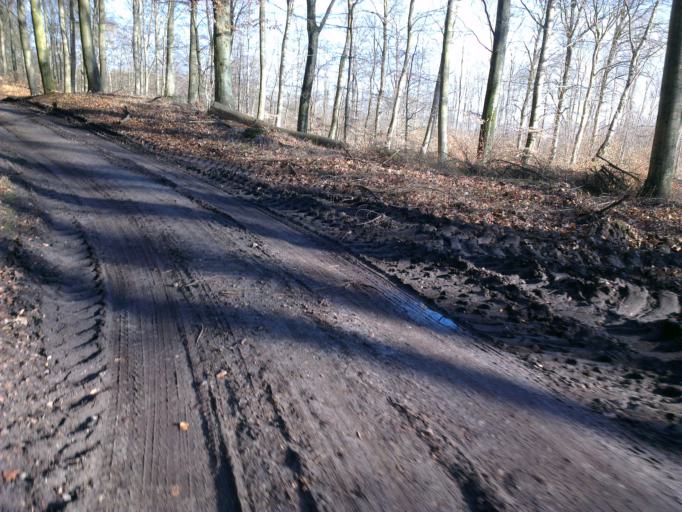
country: DK
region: Capital Region
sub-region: Halsnaes Kommune
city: Frederiksvaerk
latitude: 55.9065
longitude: 12.0119
